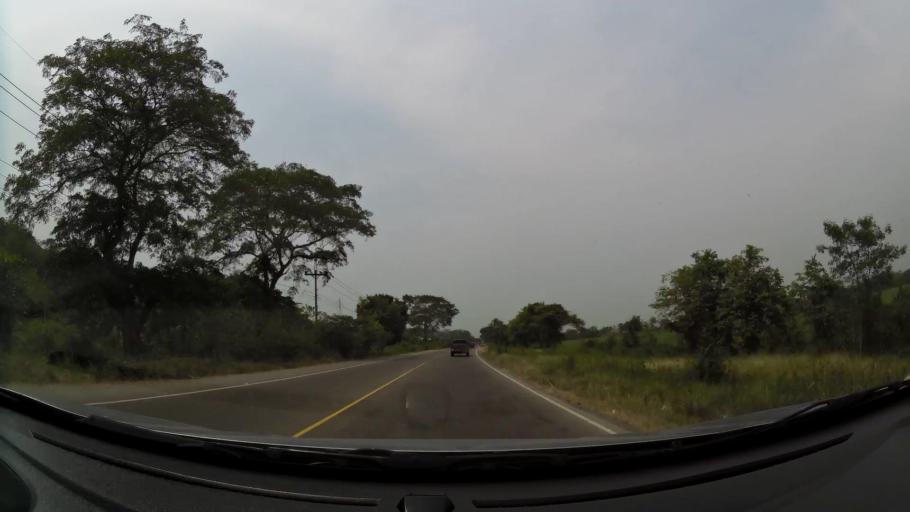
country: HN
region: Cortes
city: Potrerillos
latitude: 15.1816
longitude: -87.9622
